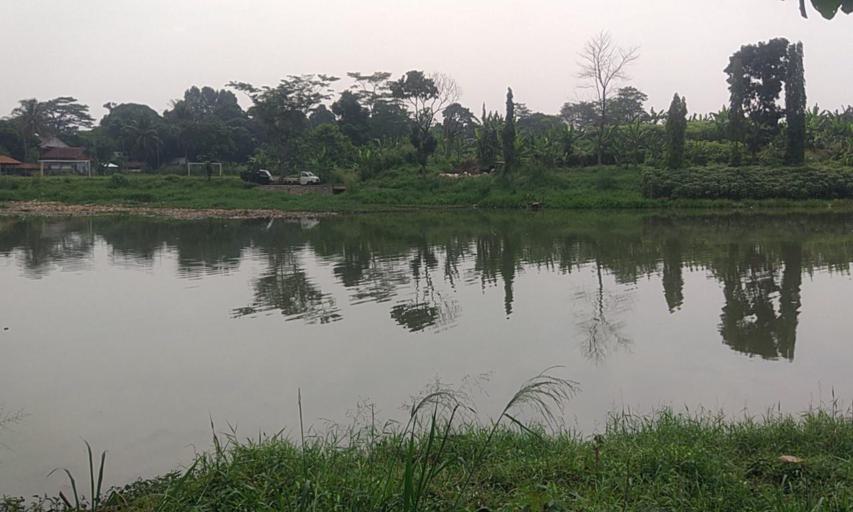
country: ID
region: West Java
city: Ciampea
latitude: -6.4962
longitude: 106.7450
